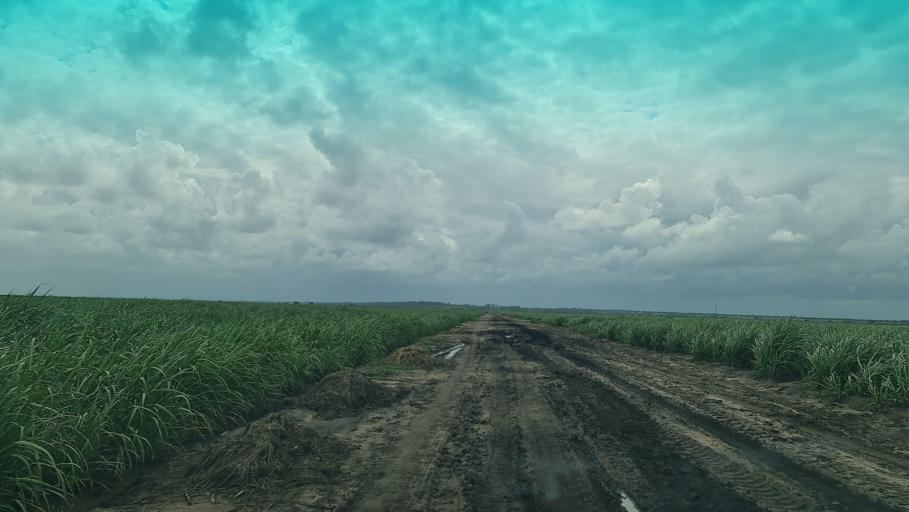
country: MZ
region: Maputo
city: Manhica
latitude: -25.4533
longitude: 32.8305
